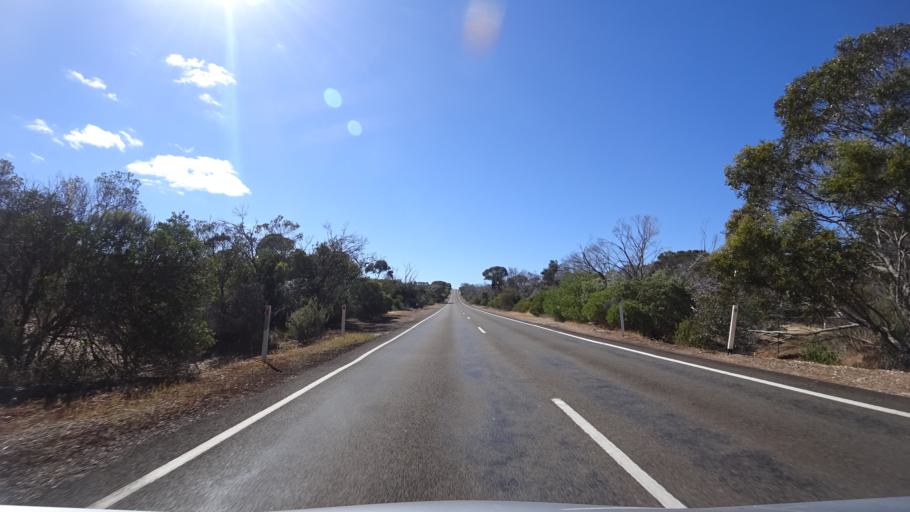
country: AU
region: South Australia
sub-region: Kangaroo Island
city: Kingscote
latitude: -35.7595
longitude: 137.6072
